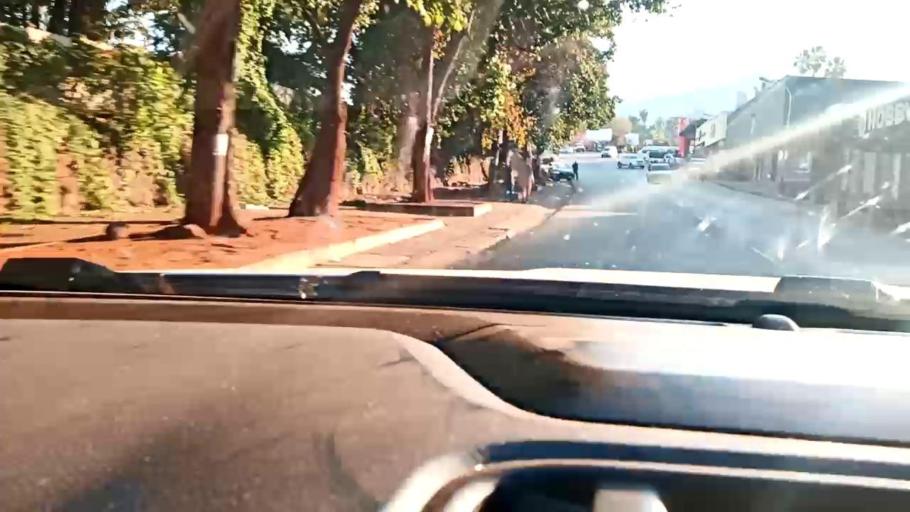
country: ZA
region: Limpopo
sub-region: Mopani District Municipality
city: Duiwelskloof
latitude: -23.6952
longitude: 30.1429
